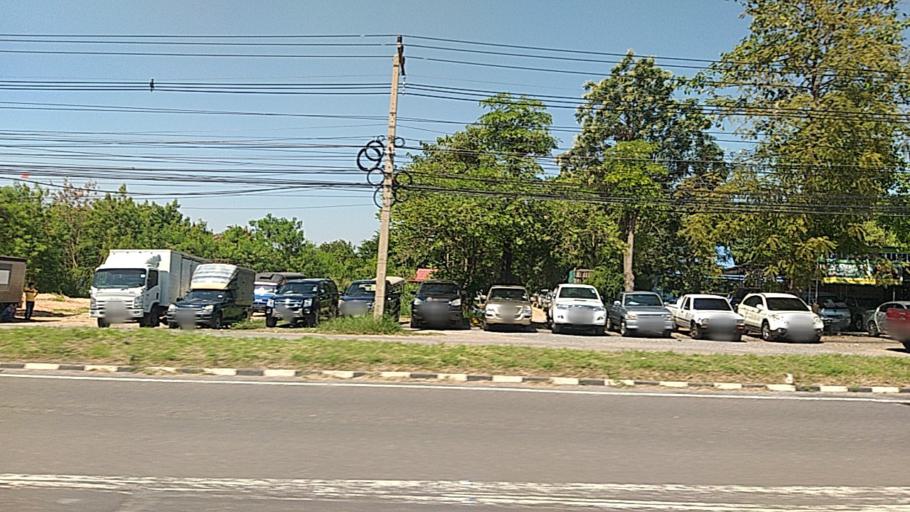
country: TH
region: Nakhon Ratchasima
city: Kham Thale So
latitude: 14.9292
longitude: 101.9714
